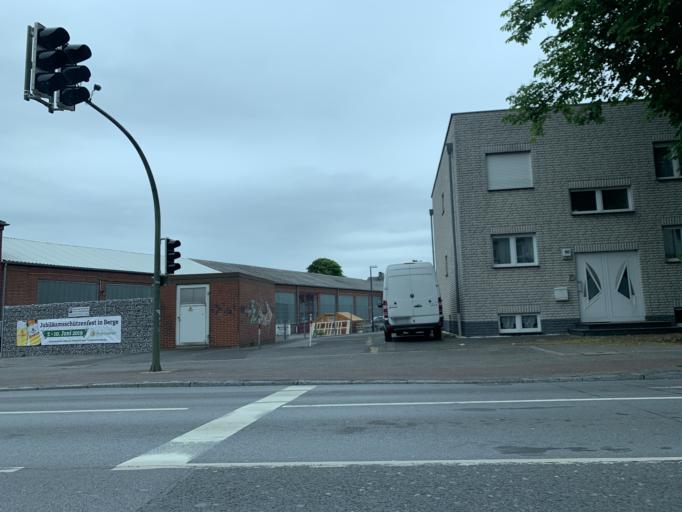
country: DE
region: North Rhine-Westphalia
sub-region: Regierungsbezirk Arnsberg
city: Hamm
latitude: 51.6656
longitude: 7.8328
